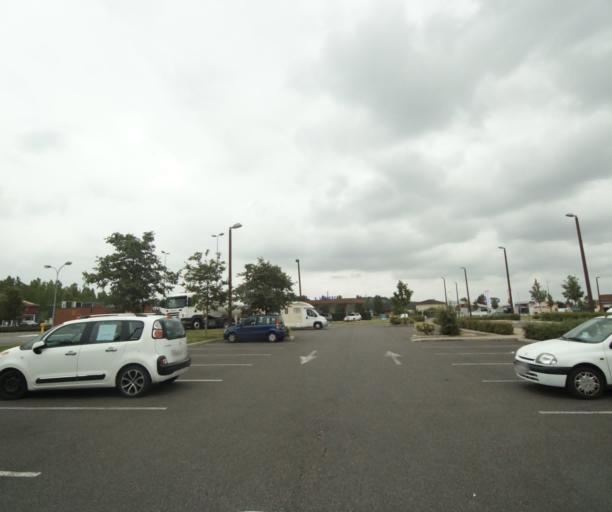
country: FR
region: Midi-Pyrenees
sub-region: Departement du Tarn-et-Garonne
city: Montauban
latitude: 44.0042
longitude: 1.3553
